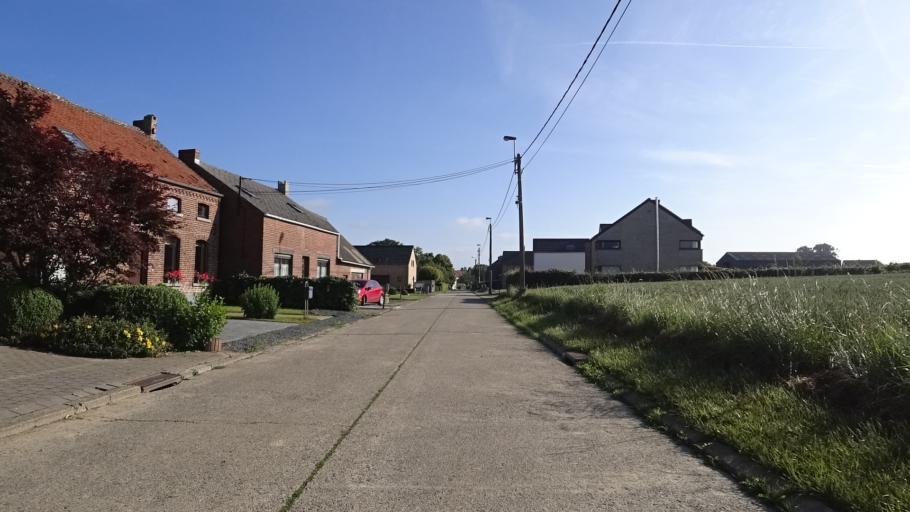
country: BE
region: Wallonia
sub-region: Province du Brabant Wallon
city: Walhain-Saint-Paul
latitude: 50.6106
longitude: 4.7199
